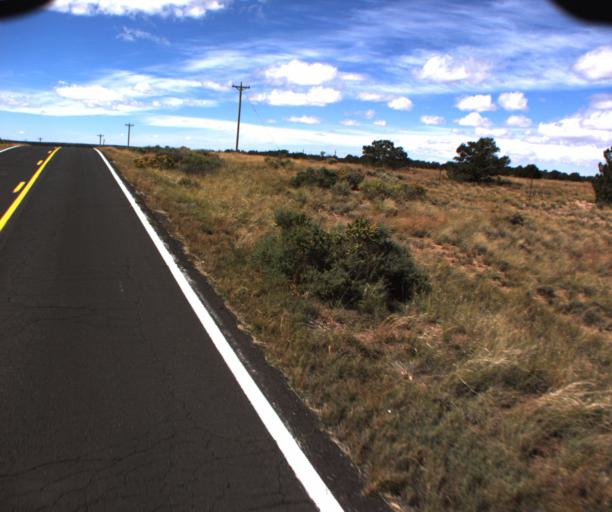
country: US
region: New Mexico
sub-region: McKinley County
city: Zuni Pueblo
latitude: 34.9882
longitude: -109.1154
